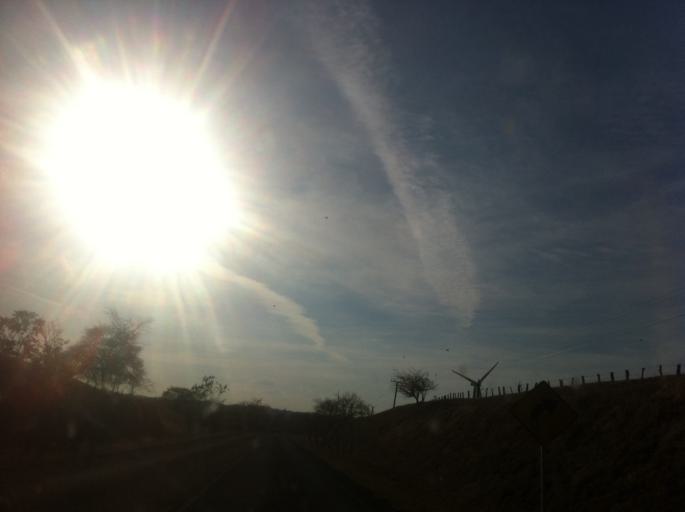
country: NI
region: Rivas
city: San Juan del Sur
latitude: 11.3040
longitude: -85.6913
